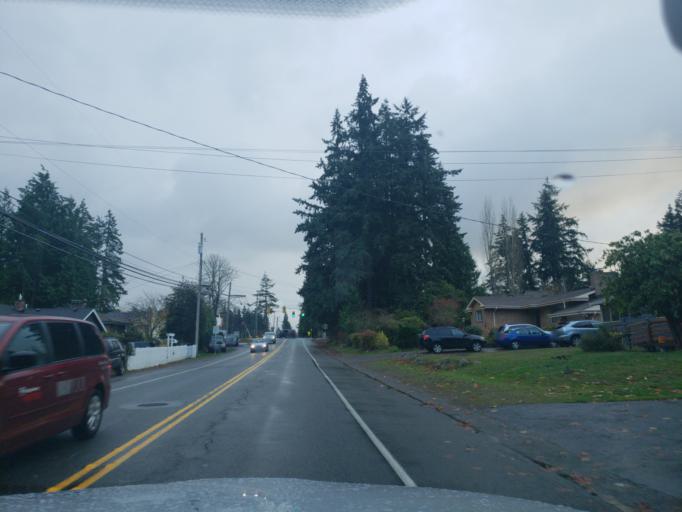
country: US
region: Washington
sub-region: King County
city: Shoreline
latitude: 47.7570
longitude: -122.3511
